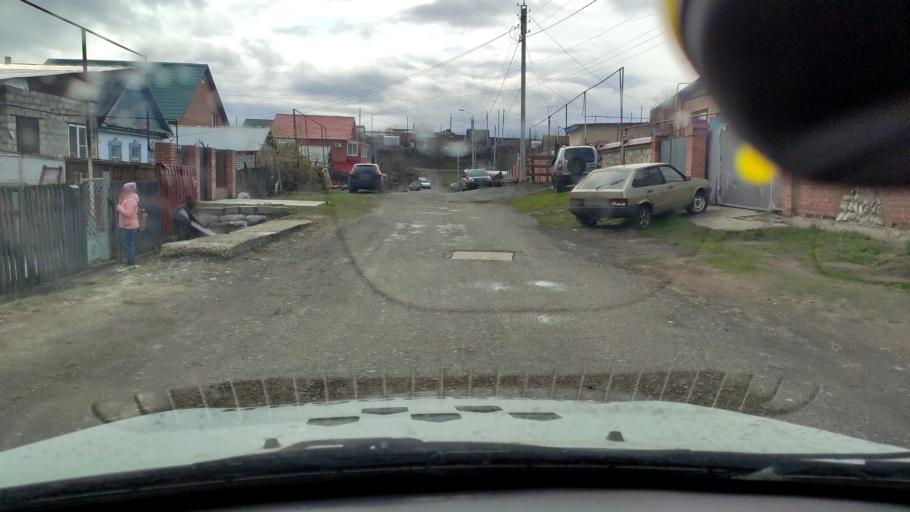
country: RU
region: Samara
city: Zhigulevsk
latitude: 53.4676
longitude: 49.6031
